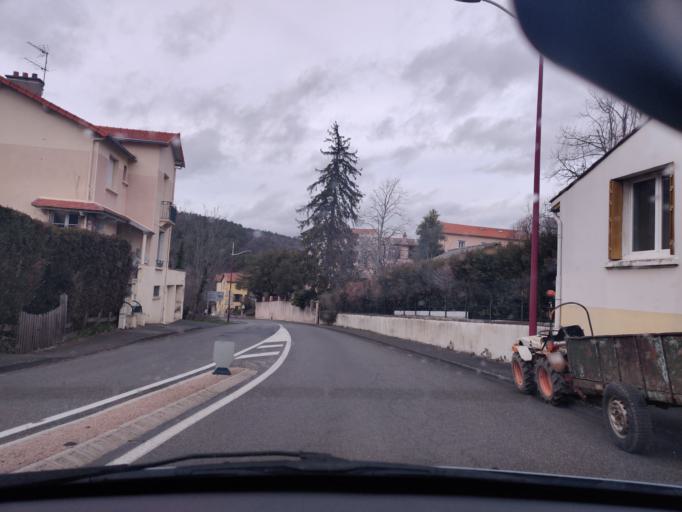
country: FR
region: Auvergne
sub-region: Departement du Puy-de-Dome
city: Chatel-Guyon
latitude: 45.9134
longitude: 3.0562
